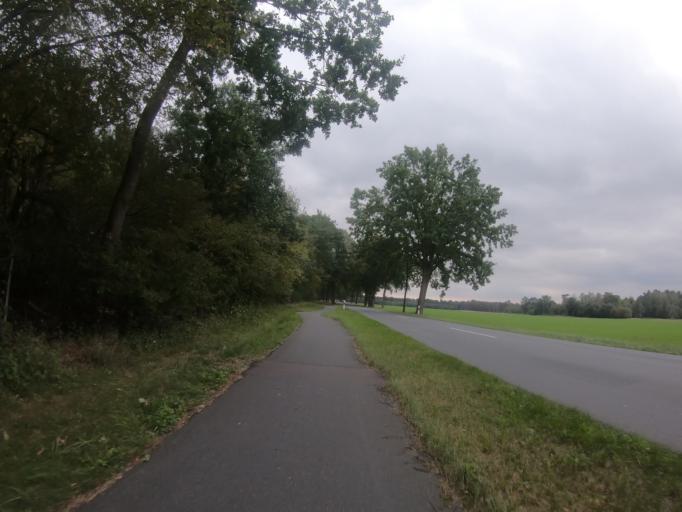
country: DE
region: Lower Saxony
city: Ribbesbuttel
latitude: 52.4445
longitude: 10.5020
